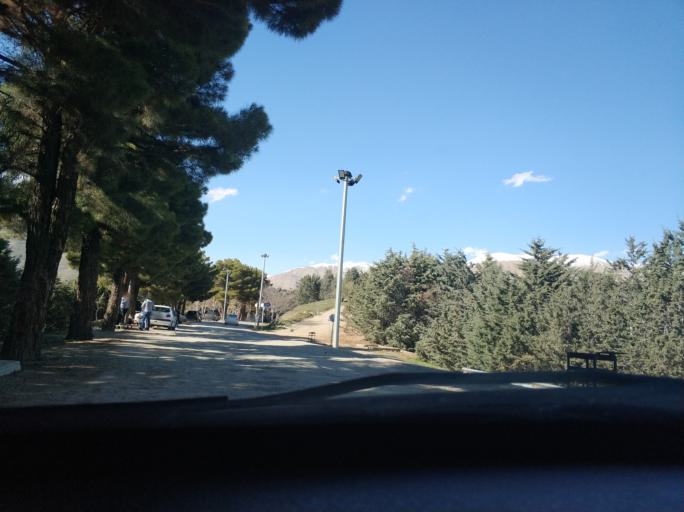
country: IR
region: Tehran
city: Tajrish
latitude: 35.8004
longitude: 51.5675
